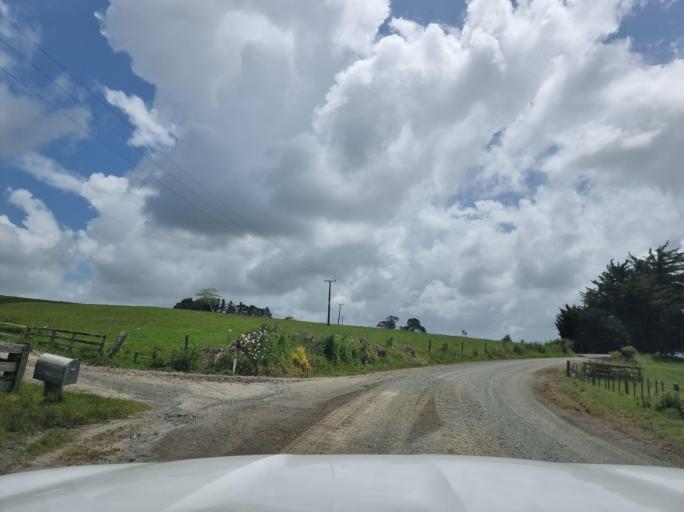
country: NZ
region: Northland
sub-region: Kaipara District
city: Dargaville
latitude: -36.1008
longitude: 174.1320
